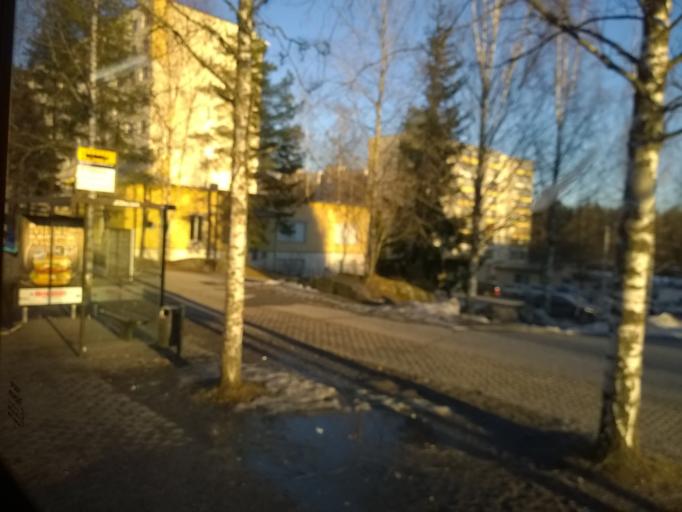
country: FI
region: Pirkanmaa
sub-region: Tampere
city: Tampere
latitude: 61.4514
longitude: 23.8388
